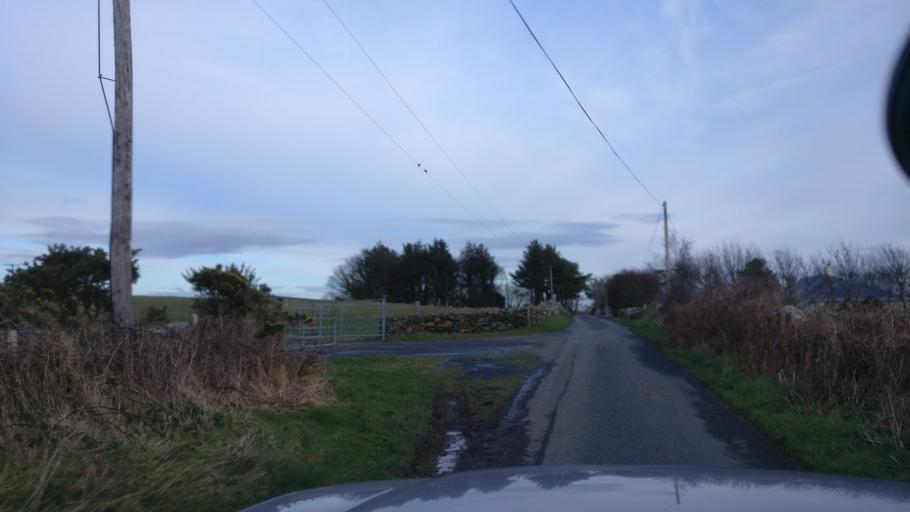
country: IE
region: Connaught
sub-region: County Galway
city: Oughterard
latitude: 53.5293
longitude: -9.3655
